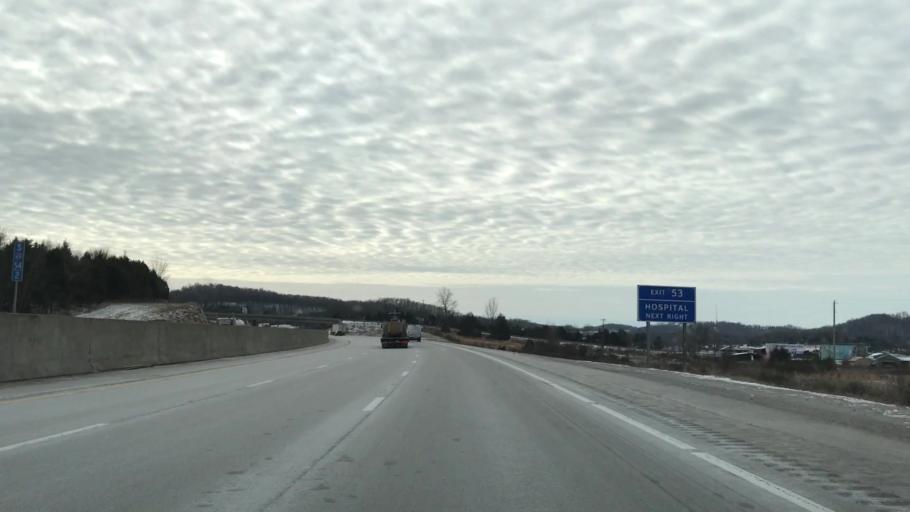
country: US
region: Kentucky
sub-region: Barren County
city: Cave City
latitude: 37.1614
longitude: -85.9692
